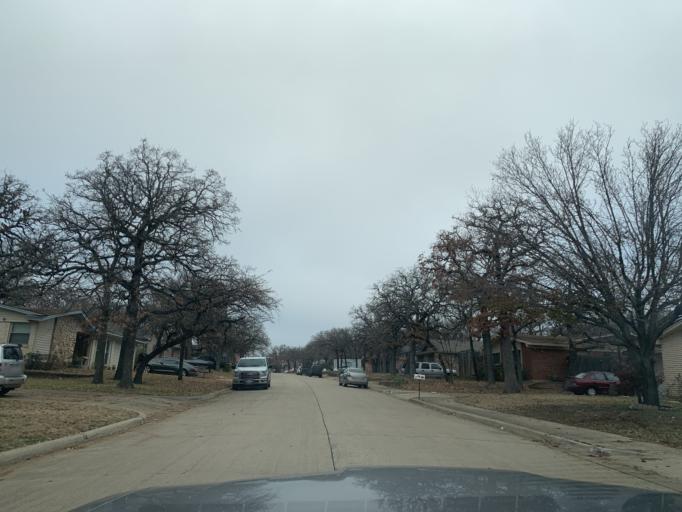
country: US
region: Texas
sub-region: Tarrant County
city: Bedford
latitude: 32.8345
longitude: -97.1554
